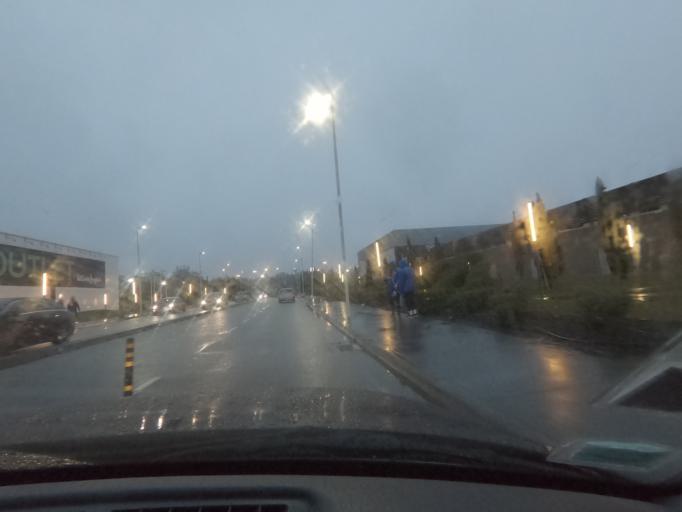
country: PT
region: Porto
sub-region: Vila do Conde
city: Arvore
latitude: 41.3003
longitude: -8.7075
